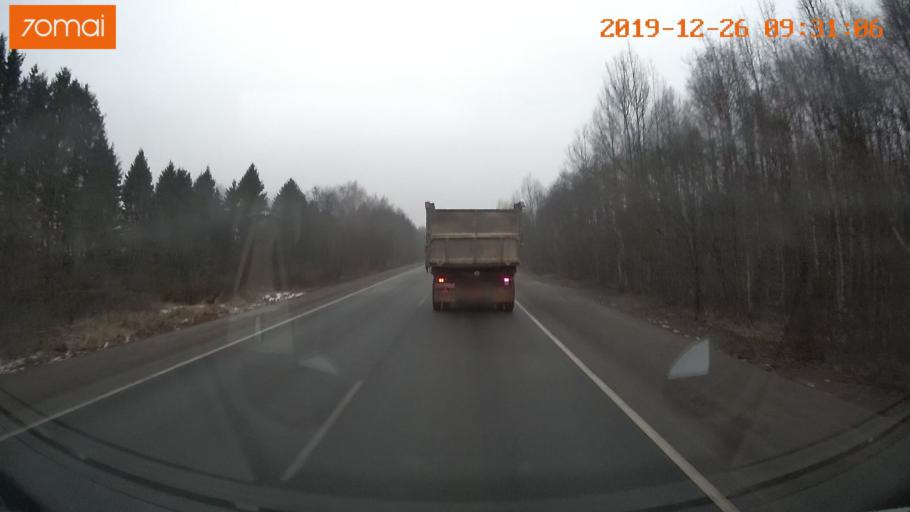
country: RU
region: Vologda
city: Gryazovets
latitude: 59.0664
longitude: 40.1316
